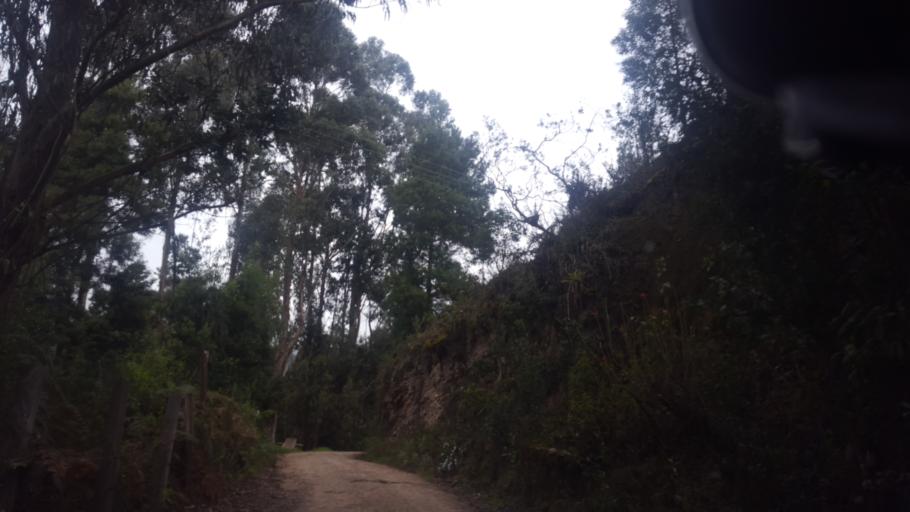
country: CO
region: Boyaca
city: Cerinza
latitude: 5.9830
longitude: -72.9441
